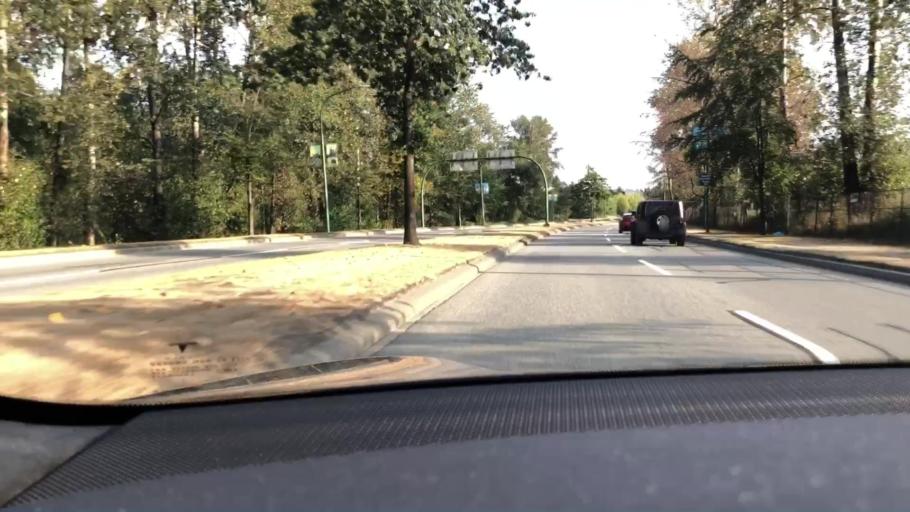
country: CA
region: British Columbia
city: Burnaby
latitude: 49.2561
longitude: -122.9673
